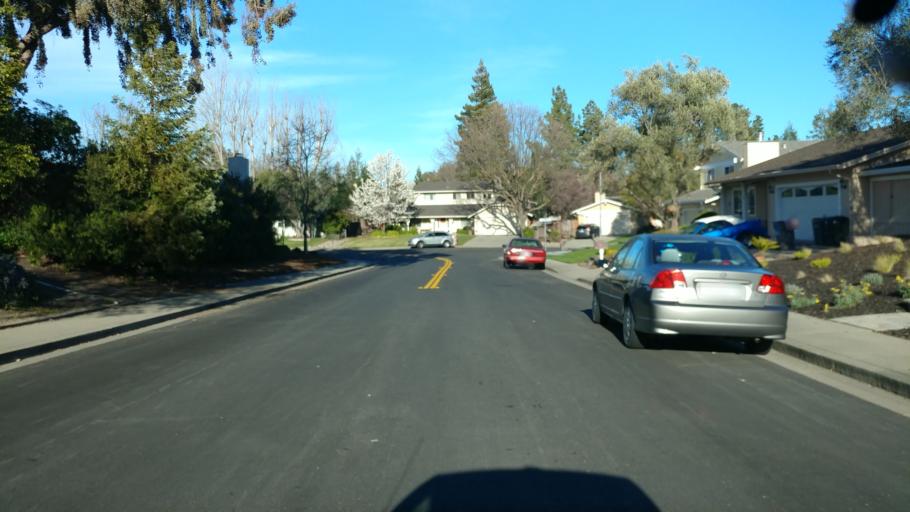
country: US
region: California
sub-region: Contra Costa County
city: San Ramon
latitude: 37.7464
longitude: -121.9592
